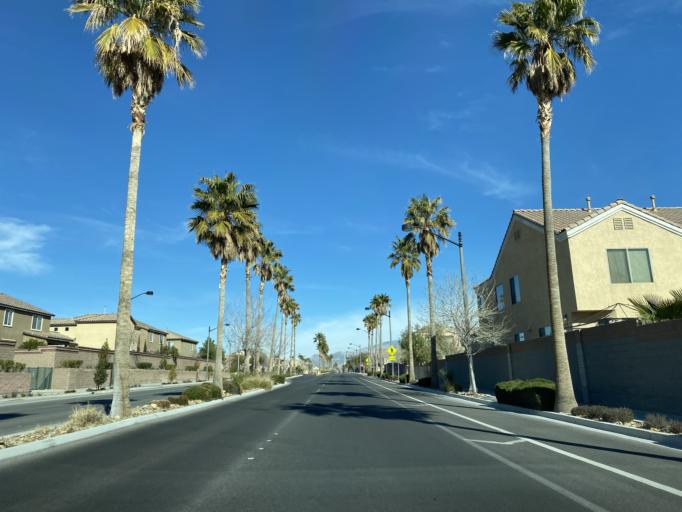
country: US
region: Nevada
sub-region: Clark County
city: Summerlin South
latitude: 36.2870
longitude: -115.2968
